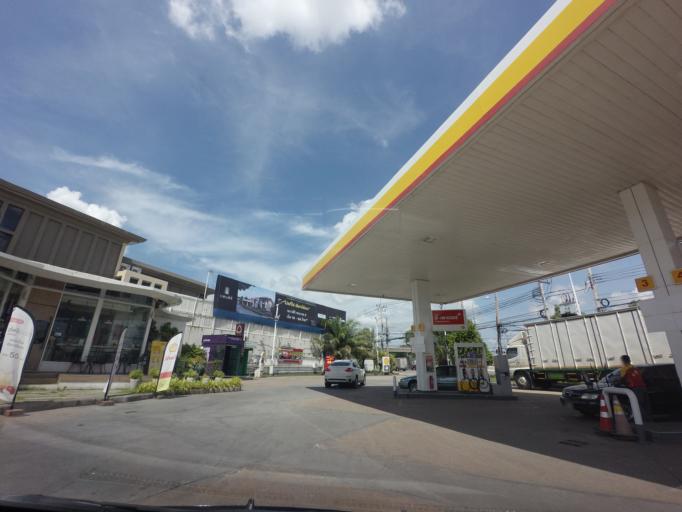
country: TH
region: Bangkok
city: Bang Bon
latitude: 13.6221
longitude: 100.3903
